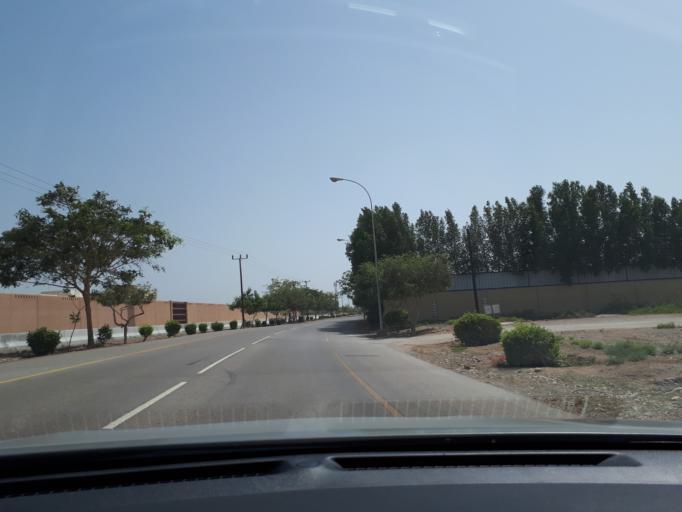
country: OM
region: Muhafazat Masqat
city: As Sib al Jadidah
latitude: 23.6995
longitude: 58.0745
